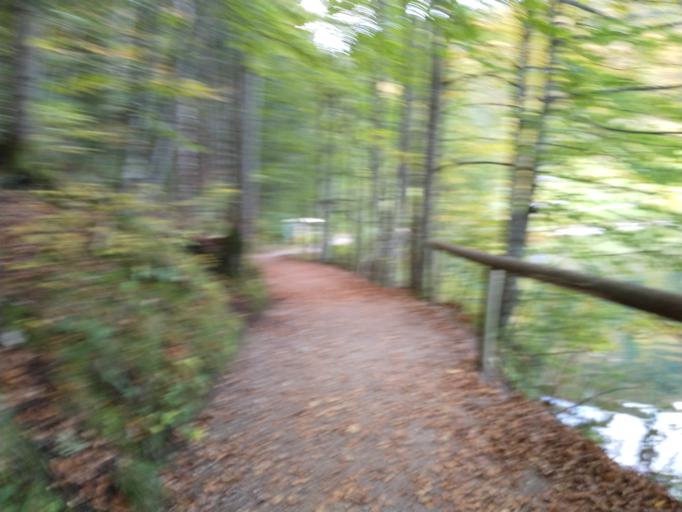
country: AT
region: Tyrol
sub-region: Politischer Bezirk Reutte
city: Vils
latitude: 47.5600
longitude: 10.6368
